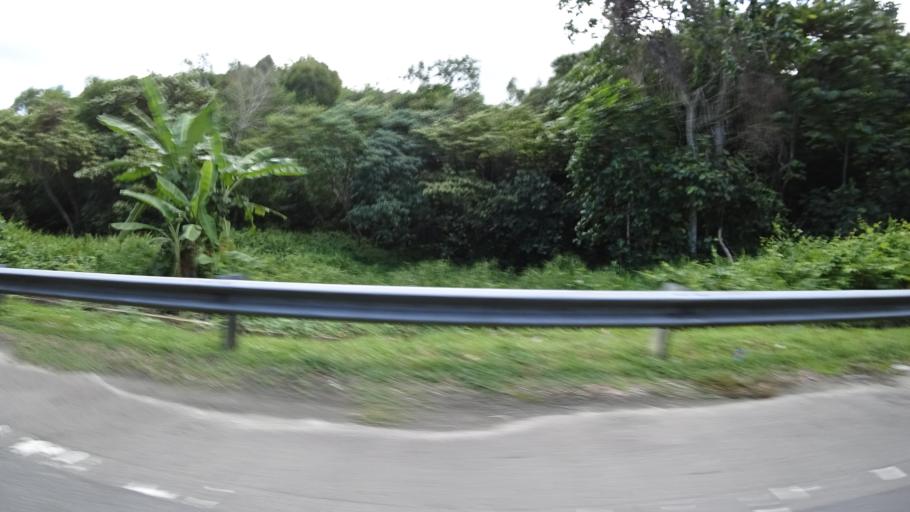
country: BN
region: Brunei and Muara
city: Bandar Seri Begawan
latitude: 4.8542
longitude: 114.9259
